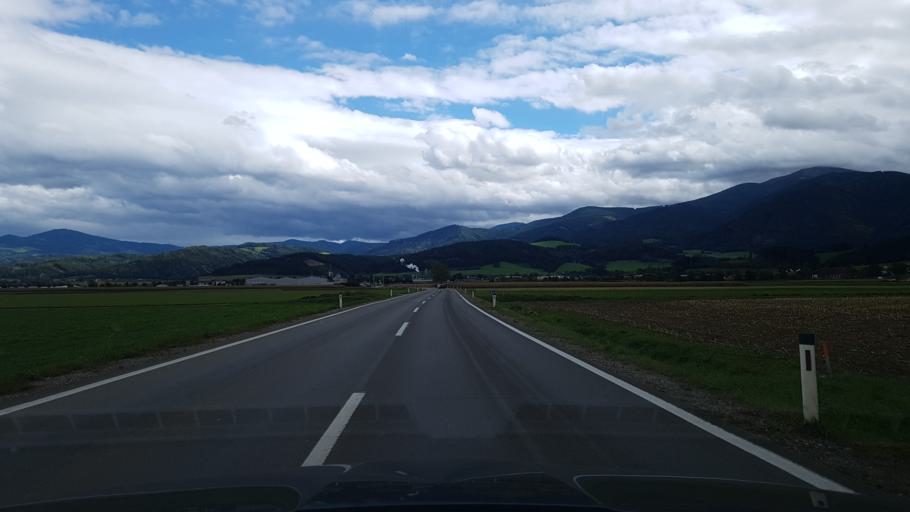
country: AT
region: Styria
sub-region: Politischer Bezirk Murtal
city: Weisskirchen in Steiermark
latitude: 47.1602
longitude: 14.7115
